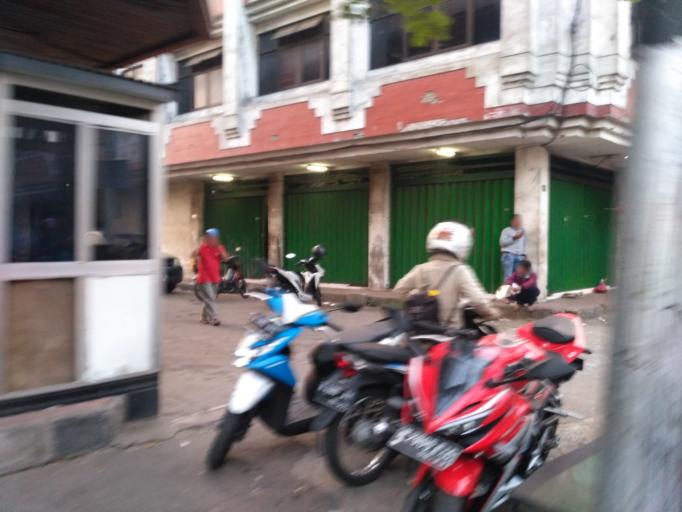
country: ID
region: East Java
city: Malang
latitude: -7.9921
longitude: 112.6339
